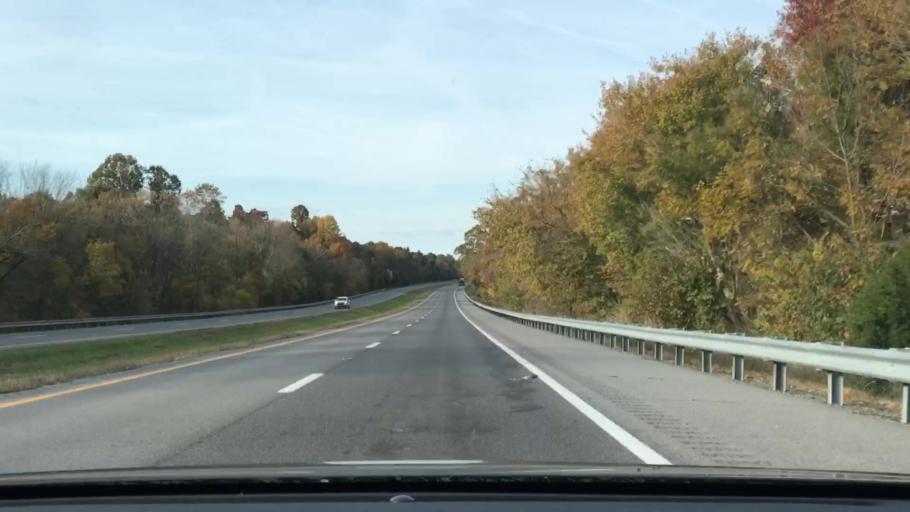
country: US
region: Kentucky
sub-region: Marshall County
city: Benton
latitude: 36.8425
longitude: -88.4142
